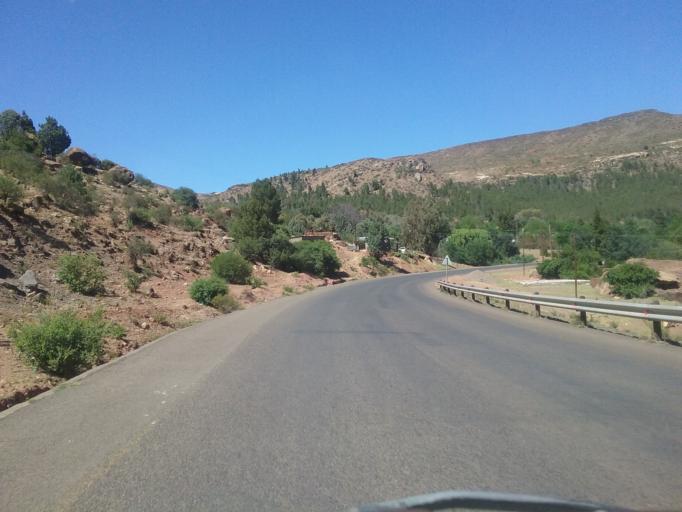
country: LS
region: Quthing
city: Quthing
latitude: -30.4018
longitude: 27.6848
